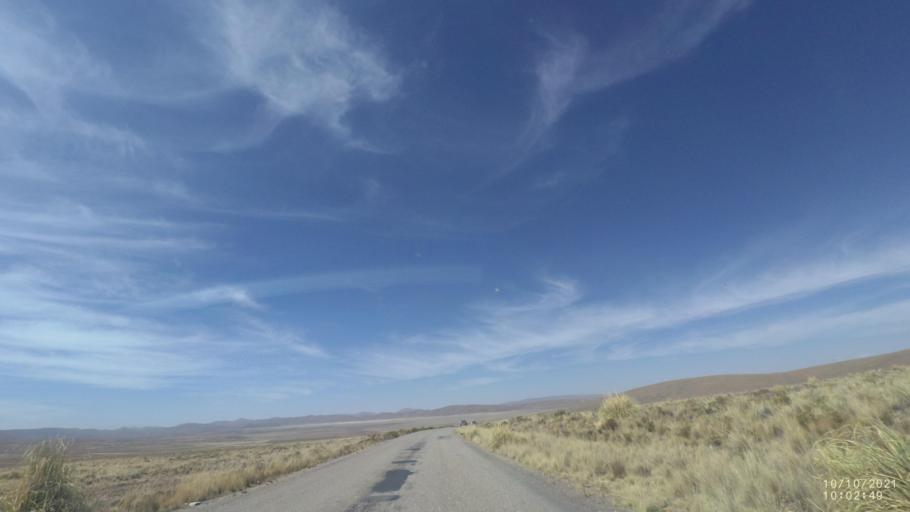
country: BO
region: La Paz
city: Eucaliptus
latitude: -17.3613
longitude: -67.4369
